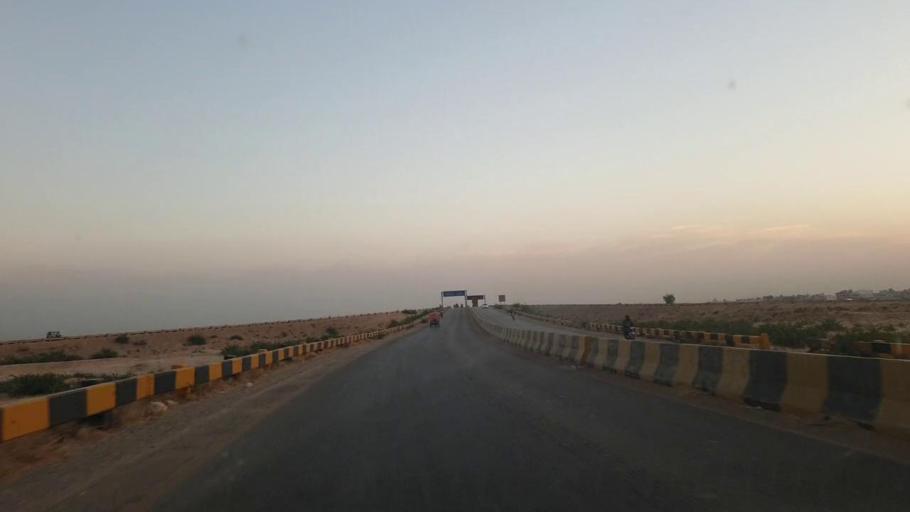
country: PK
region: Sindh
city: Jamshoro
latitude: 25.4030
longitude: 68.2719
